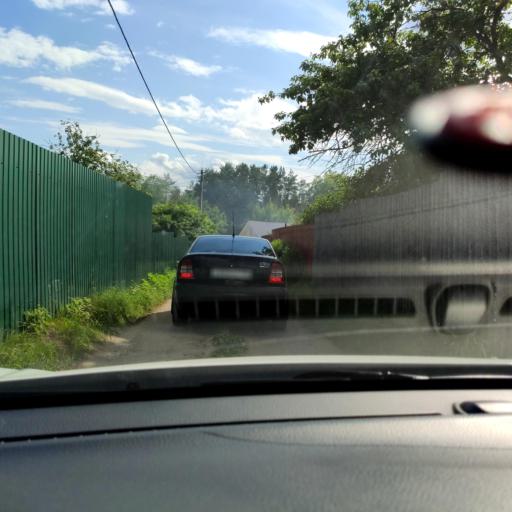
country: RU
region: Tatarstan
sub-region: Gorod Kazan'
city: Kazan
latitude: 55.8891
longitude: 49.0574
